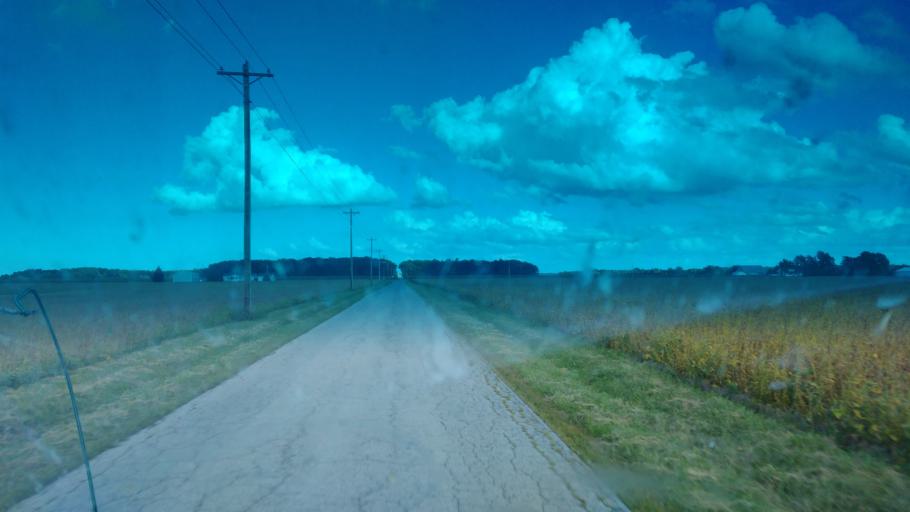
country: US
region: Ohio
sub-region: Hancock County
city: Arlington
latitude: 40.9363
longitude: -83.7328
